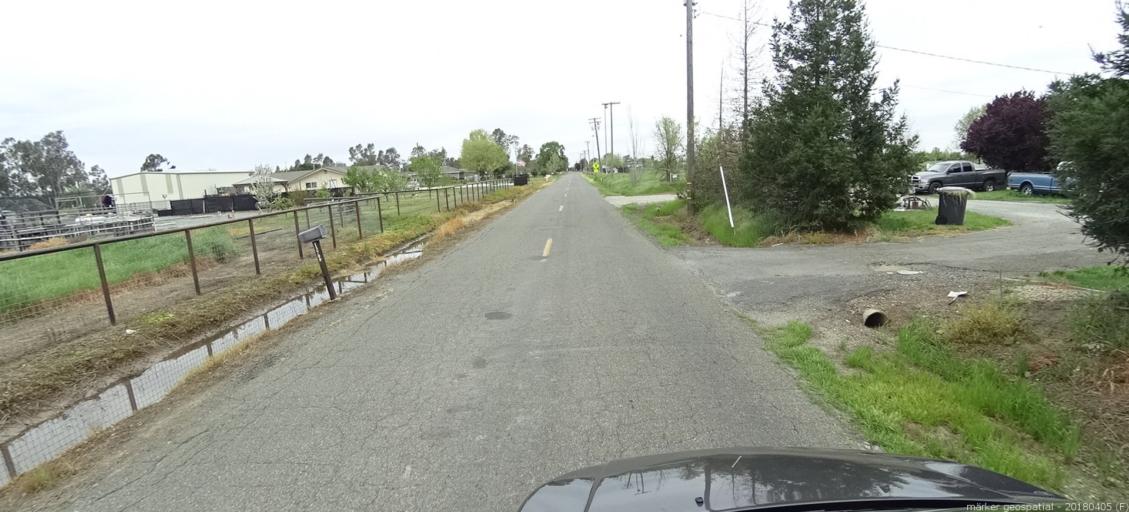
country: US
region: California
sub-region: Sacramento County
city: Galt
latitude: 38.2578
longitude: -121.3261
